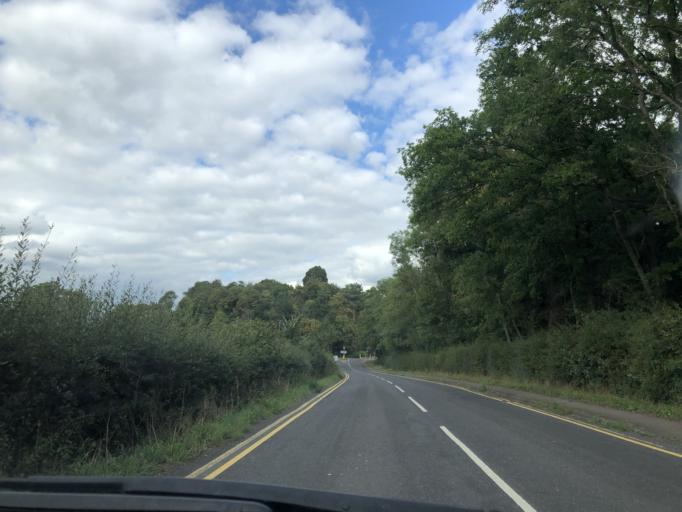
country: GB
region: England
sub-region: Kent
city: Tonbridge
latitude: 51.2203
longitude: 0.2290
